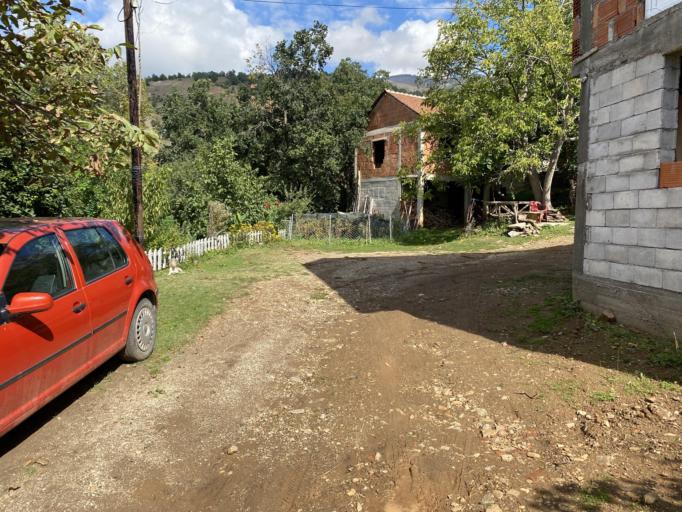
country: MK
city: Radishani
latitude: 42.1064
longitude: 21.4582
